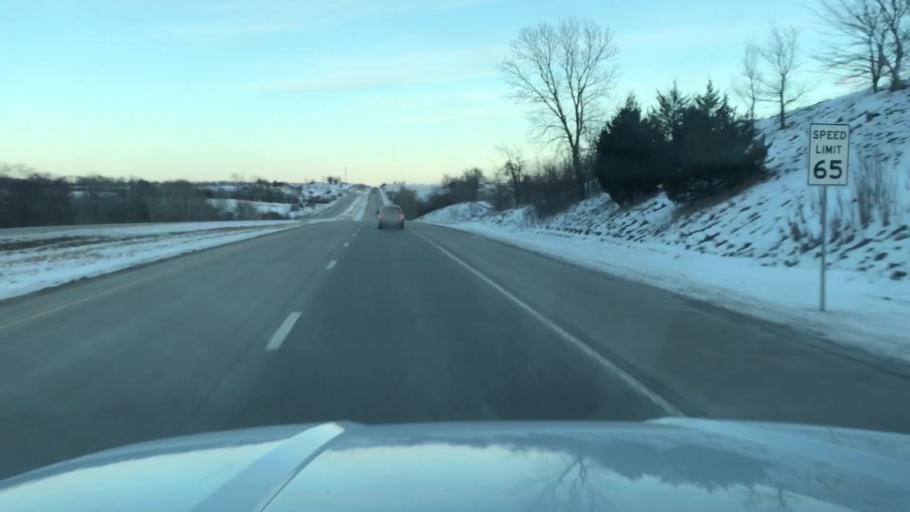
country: US
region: Missouri
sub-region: Clinton County
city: Gower
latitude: 39.7610
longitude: -94.5659
